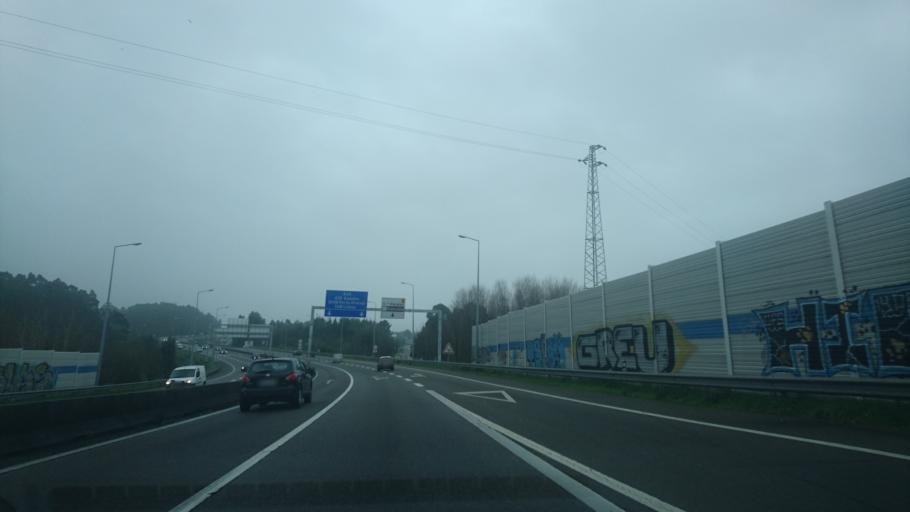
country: PT
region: Porto
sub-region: Vila Nova de Gaia
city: Gulpilhares
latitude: 41.0909
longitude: -8.6307
